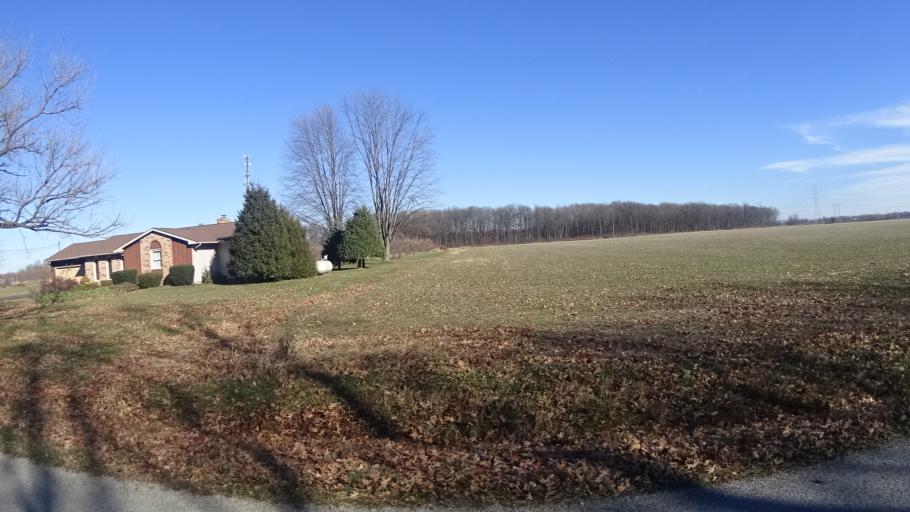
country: US
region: Ohio
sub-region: Lorain County
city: South Amherst
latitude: 41.3613
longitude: -82.2979
